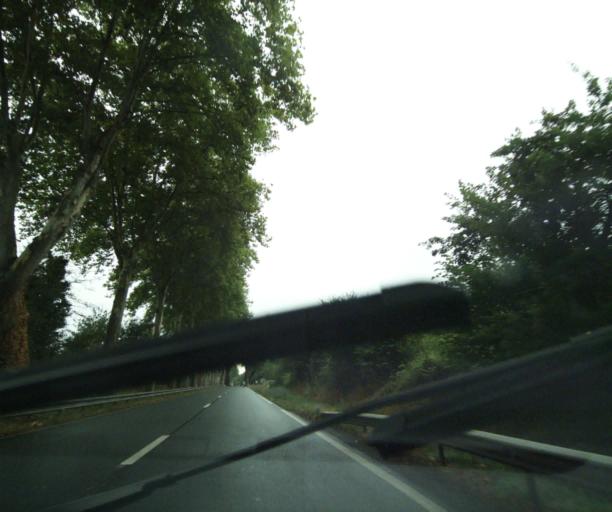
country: FR
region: Midi-Pyrenees
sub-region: Departement du Tarn
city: Arthes
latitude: 43.9746
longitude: 2.1801
